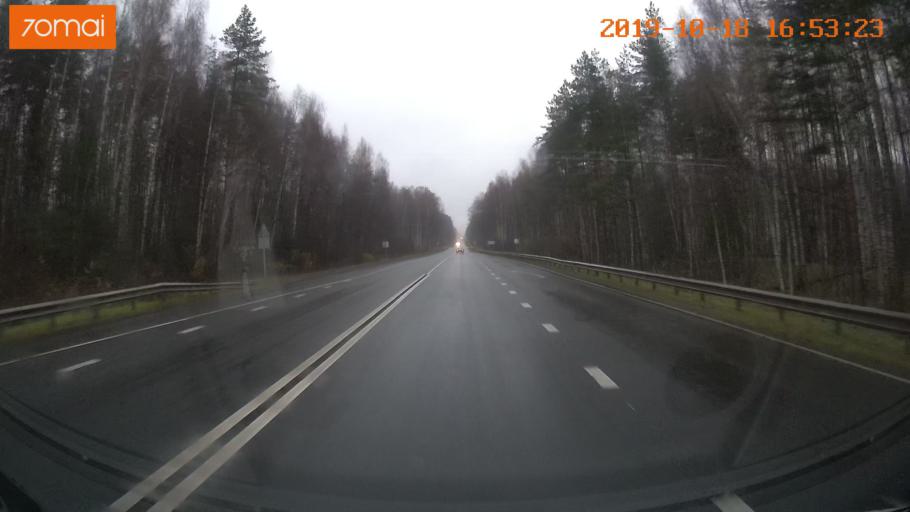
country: RU
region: Ivanovo
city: Nerl'
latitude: 56.6143
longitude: 40.5598
